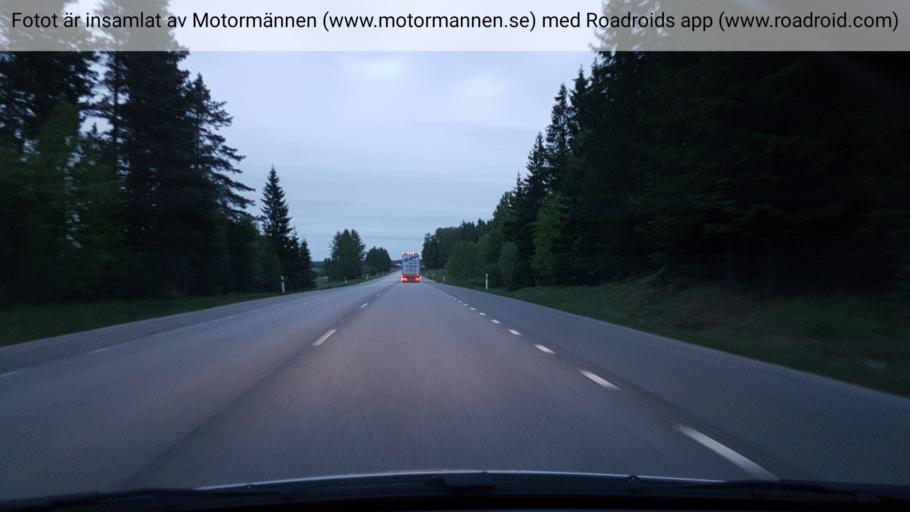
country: SE
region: Vaestmanland
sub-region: Sala Kommun
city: Sala
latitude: 59.9227
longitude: 16.6585
